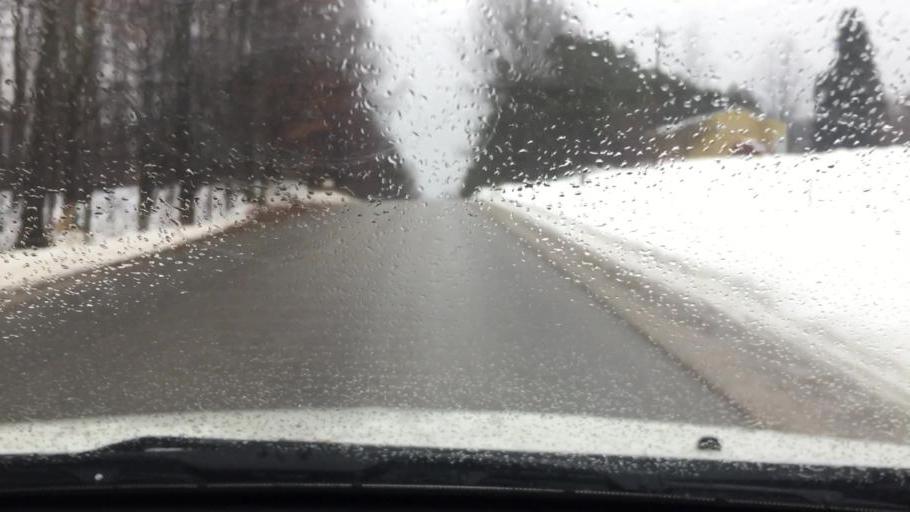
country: US
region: Michigan
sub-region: Charlevoix County
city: East Jordan
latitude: 45.1057
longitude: -85.1570
